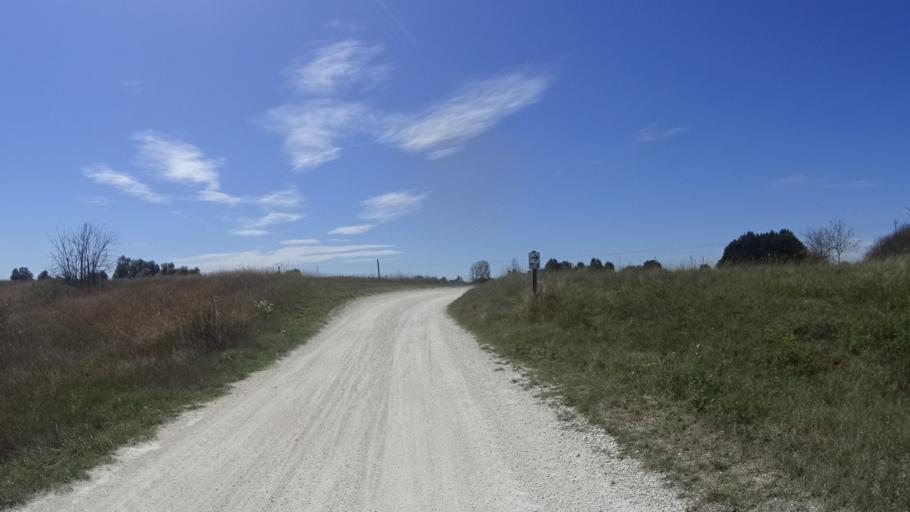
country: FR
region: Centre
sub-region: Departement du Loiret
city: Bonny-sur-Loire
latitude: 47.5344
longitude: 2.8471
